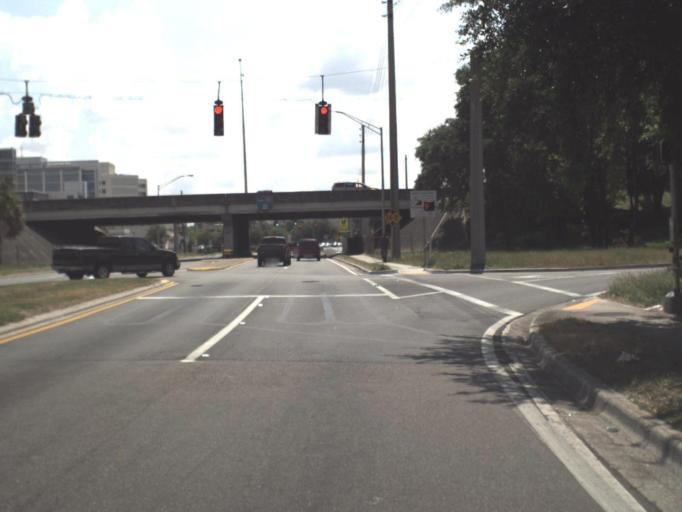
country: US
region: Florida
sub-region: Duval County
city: Jacksonville
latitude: 30.3473
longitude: -81.6695
